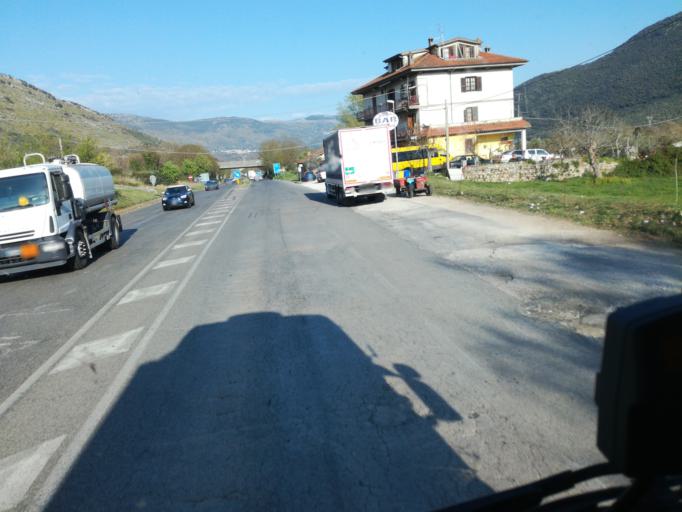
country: IT
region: Latium
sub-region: Provincia di Latina
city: Prossedi
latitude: 41.5048
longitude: 13.2371
